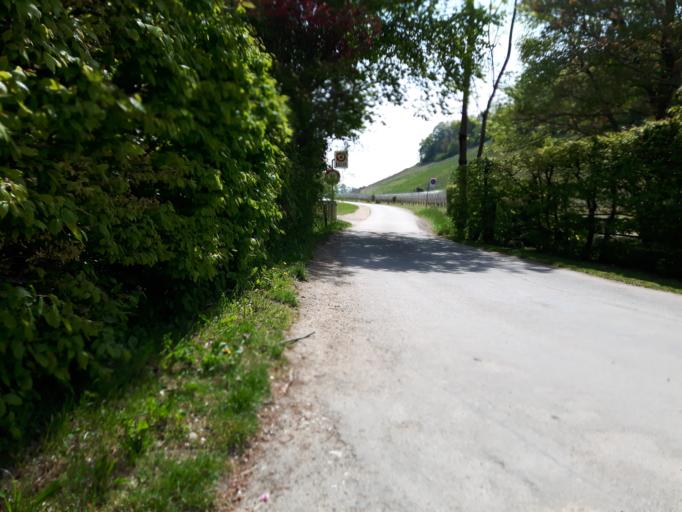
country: CH
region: Neuchatel
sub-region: Boudry District
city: Cortaillod
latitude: 46.9327
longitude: 6.8389
